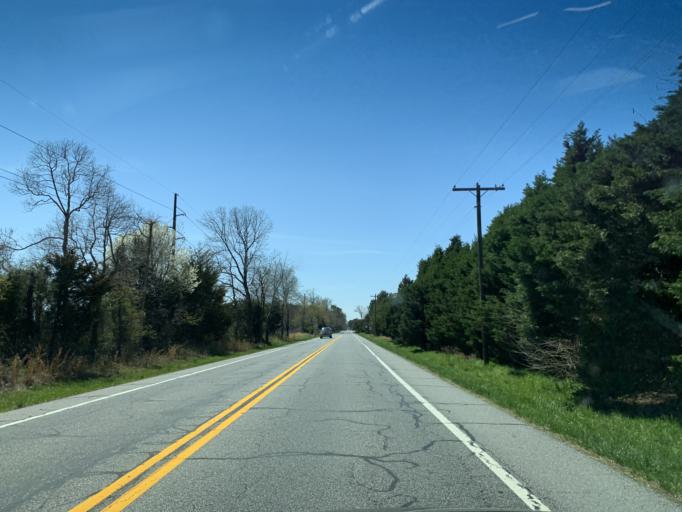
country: US
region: Maryland
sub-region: Talbot County
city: Easton
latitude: 38.8614
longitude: -76.0077
